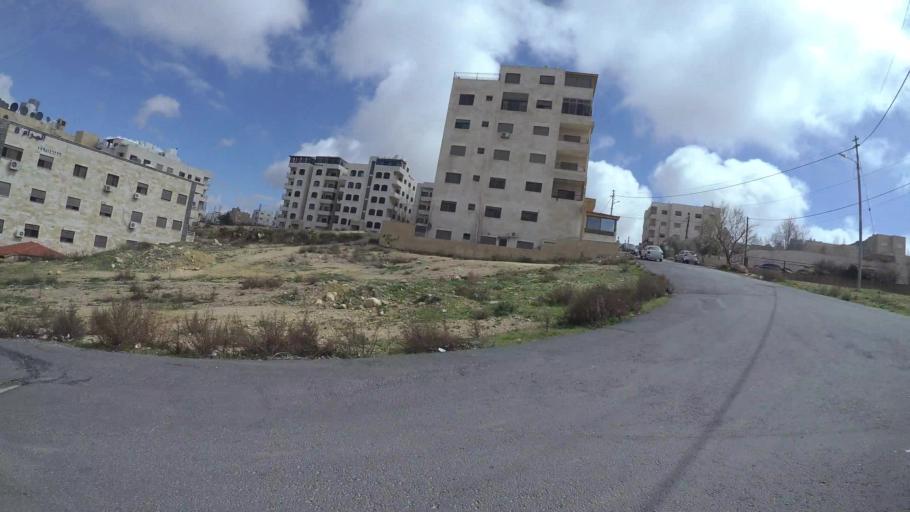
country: JO
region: Amman
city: Al Jubayhah
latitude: 32.0633
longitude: 35.8732
